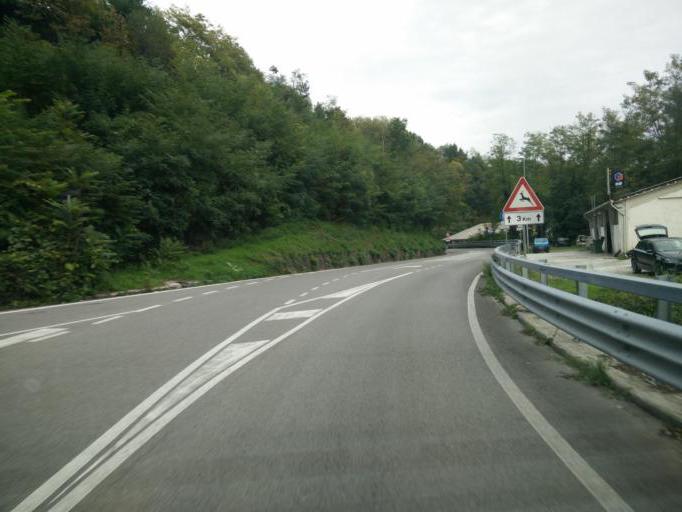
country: IT
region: Tuscany
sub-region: Provincia di Lucca
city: Piazza al Serchio-San Michele
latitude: 44.1777
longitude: 10.3121
